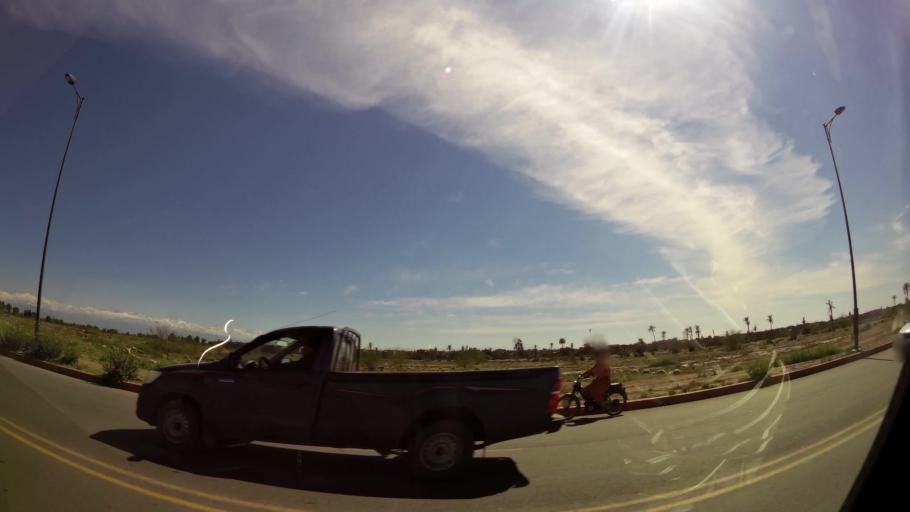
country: MA
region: Marrakech-Tensift-Al Haouz
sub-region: Marrakech
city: Marrakesh
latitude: 31.6187
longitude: -7.9586
